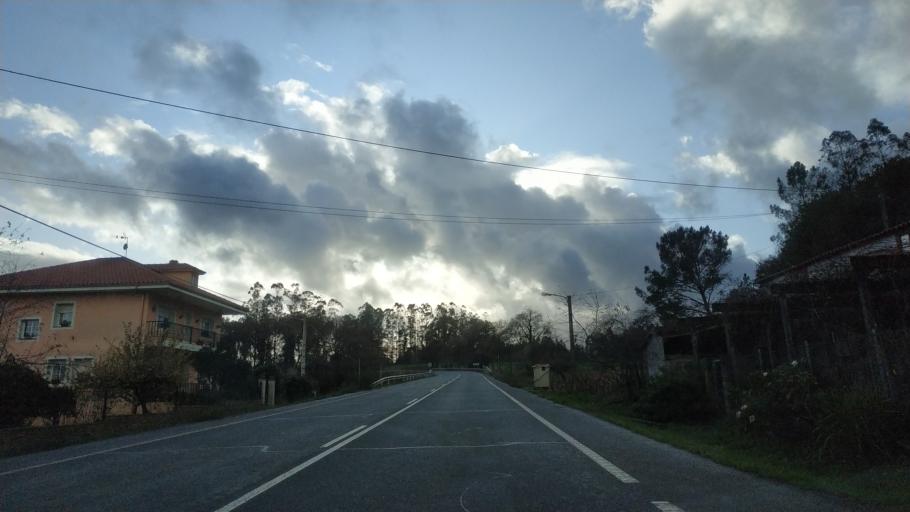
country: ES
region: Galicia
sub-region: Provincia da Coruna
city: Arzua
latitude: 42.8786
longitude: -8.2028
